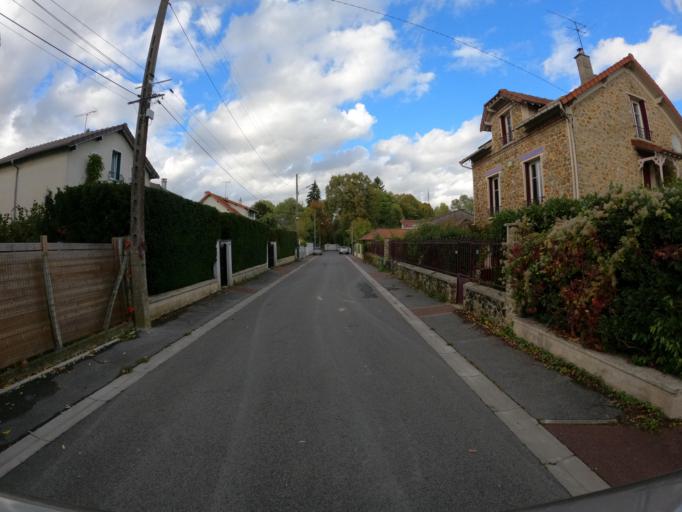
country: FR
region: Ile-de-France
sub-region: Departement de Seine-et-Marne
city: Esbly
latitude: 48.9029
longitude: 2.8174
